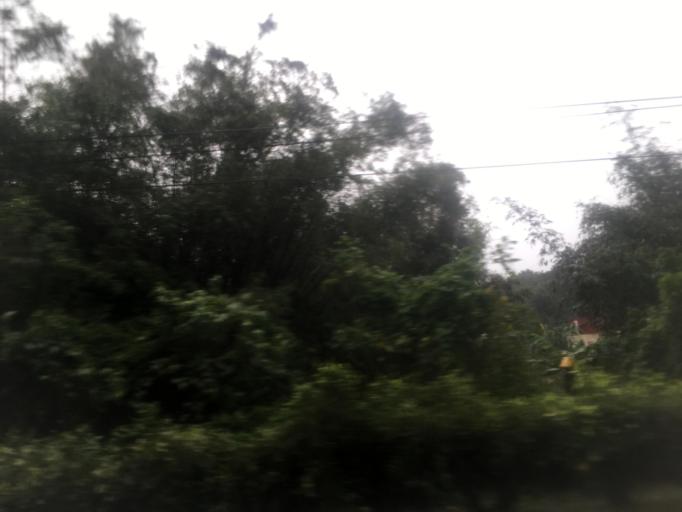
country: TW
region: Taiwan
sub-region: Keelung
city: Keelung
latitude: 25.0539
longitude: 121.9216
